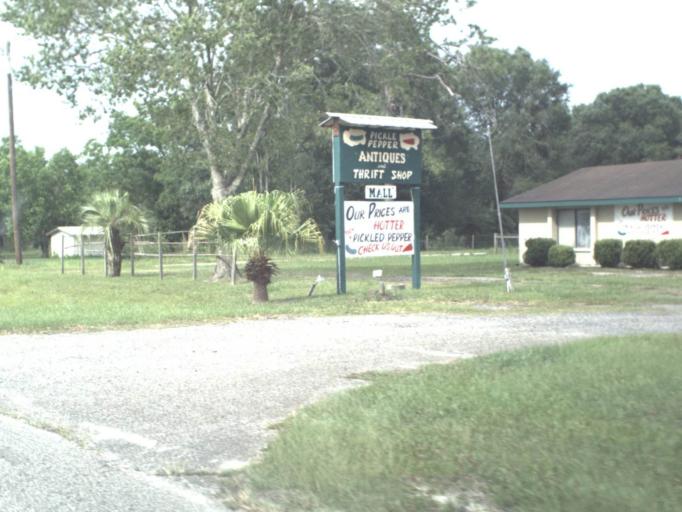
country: US
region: Florida
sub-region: Bradford County
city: Starke
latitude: 30.0043
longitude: -82.0909
